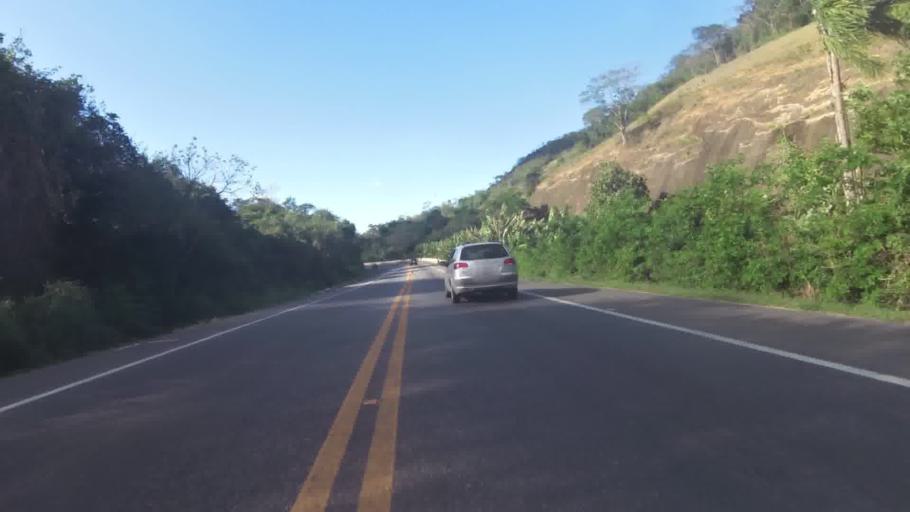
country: BR
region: Espirito Santo
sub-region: Rio Novo Do Sul
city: Rio Novo do Sul
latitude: -20.8501
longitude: -40.8764
